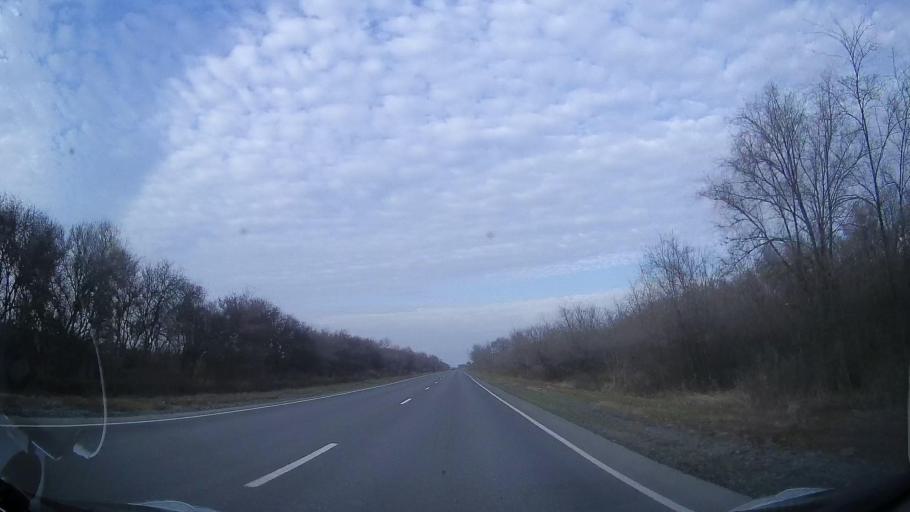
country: RU
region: Rostov
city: Bagayevskaya
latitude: 47.1298
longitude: 40.2767
